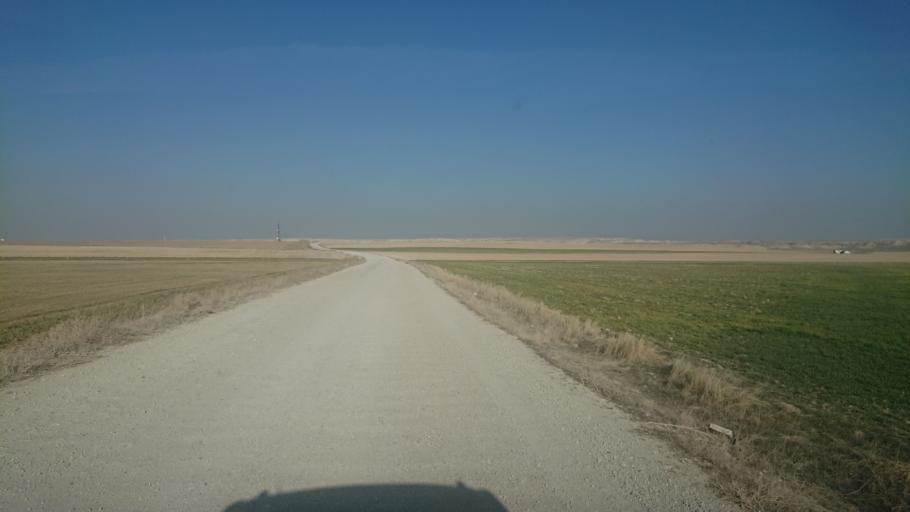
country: TR
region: Aksaray
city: Sultanhani
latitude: 38.0481
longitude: 33.6090
